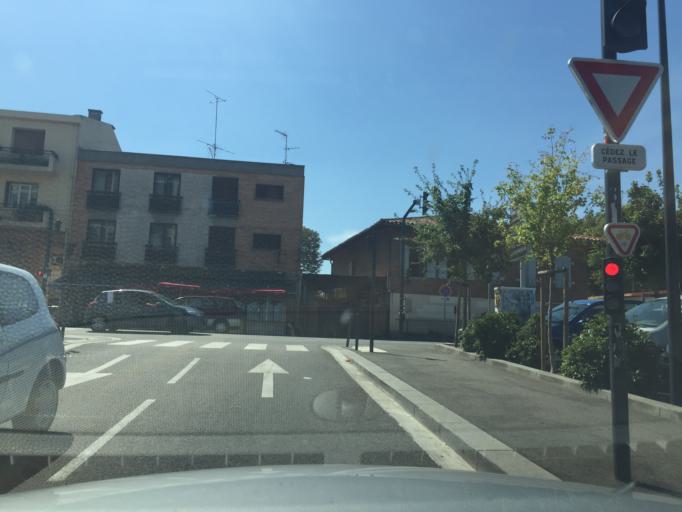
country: FR
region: Midi-Pyrenees
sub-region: Departement de la Haute-Garonne
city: Ramonville-Saint-Agne
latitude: 43.5523
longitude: 1.4695
